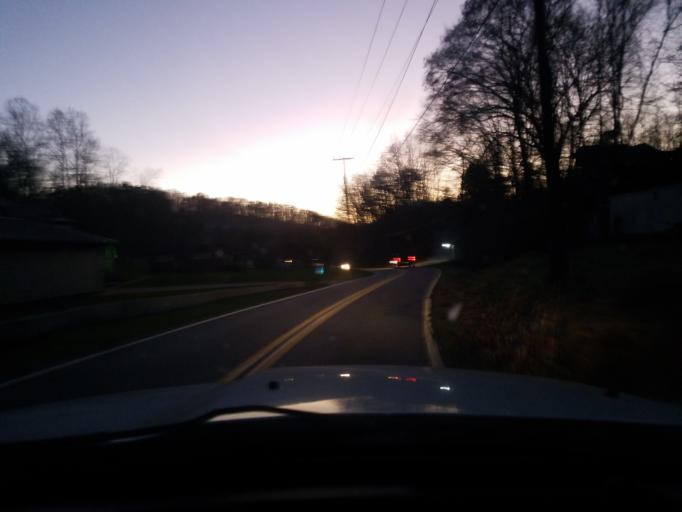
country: US
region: West Virginia
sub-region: Cabell County
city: Milton
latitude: 38.4573
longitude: -82.1107
